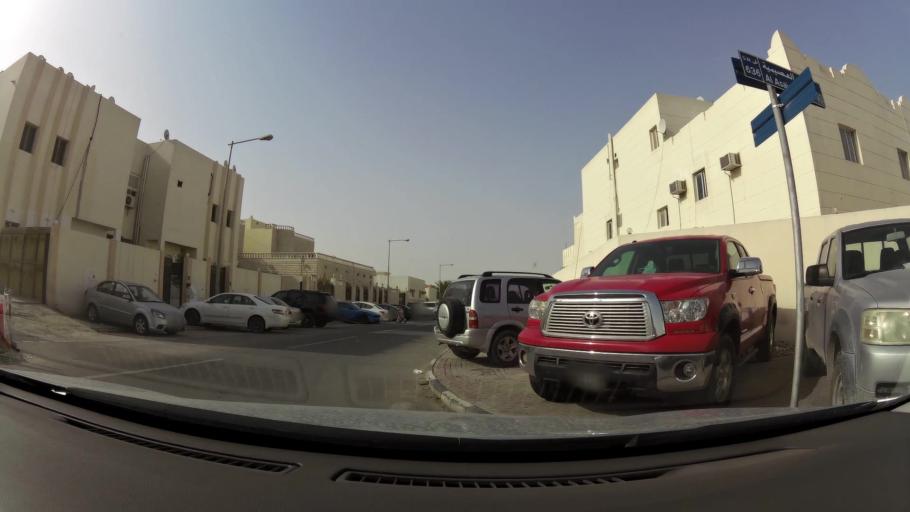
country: QA
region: Baladiyat ar Rayyan
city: Ar Rayyan
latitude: 25.2354
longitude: 51.4387
